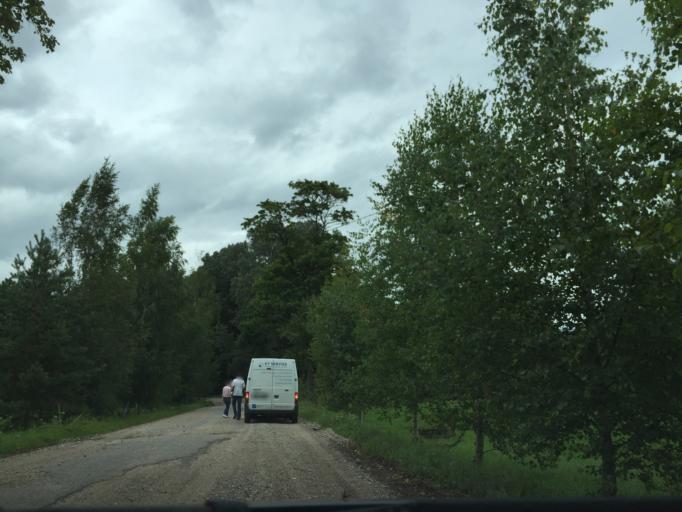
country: LV
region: Seja
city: Loja
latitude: 57.1452
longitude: 24.6626
